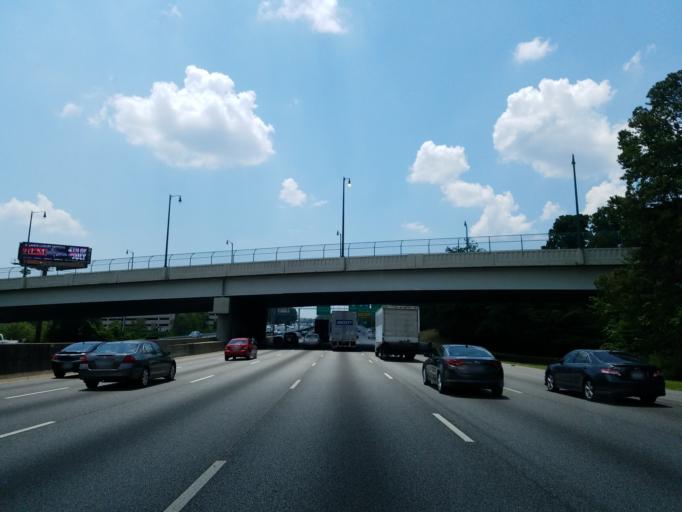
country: US
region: Georgia
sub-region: DeKalb County
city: Dunwoody
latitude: 33.9157
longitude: -84.3464
